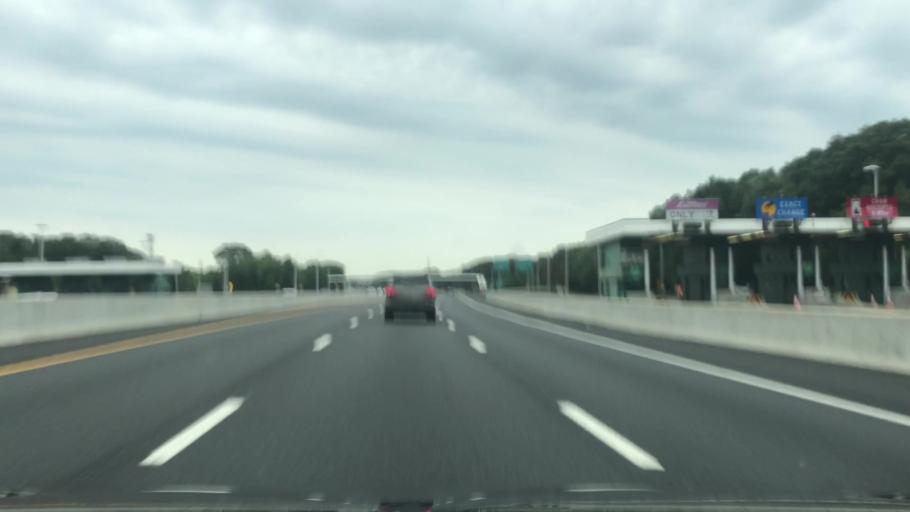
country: US
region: New Jersey
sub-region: Monmouth County
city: Ramtown
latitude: 40.1027
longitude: -74.1387
